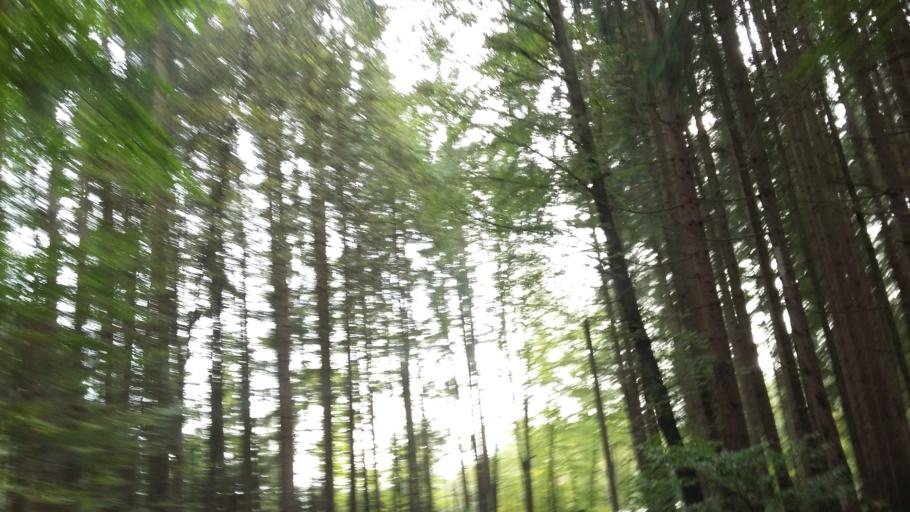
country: DE
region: Bavaria
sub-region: Upper Bavaria
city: Munsing
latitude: 47.9219
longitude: 11.3826
